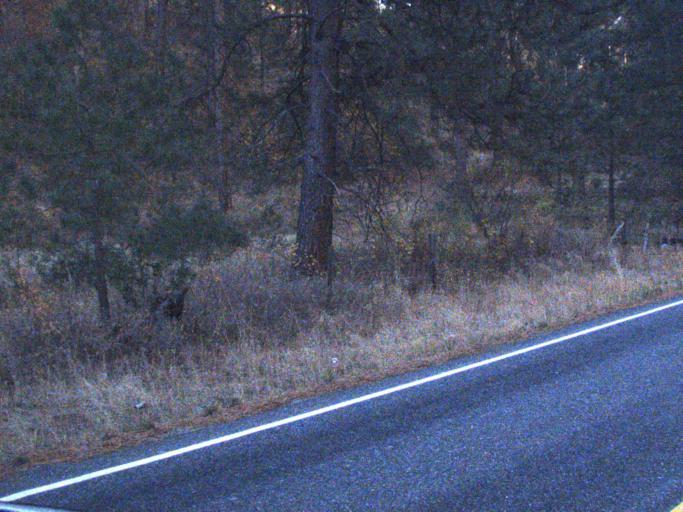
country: US
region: Washington
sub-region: Stevens County
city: Kettle Falls
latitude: 48.7289
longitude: -118.0444
